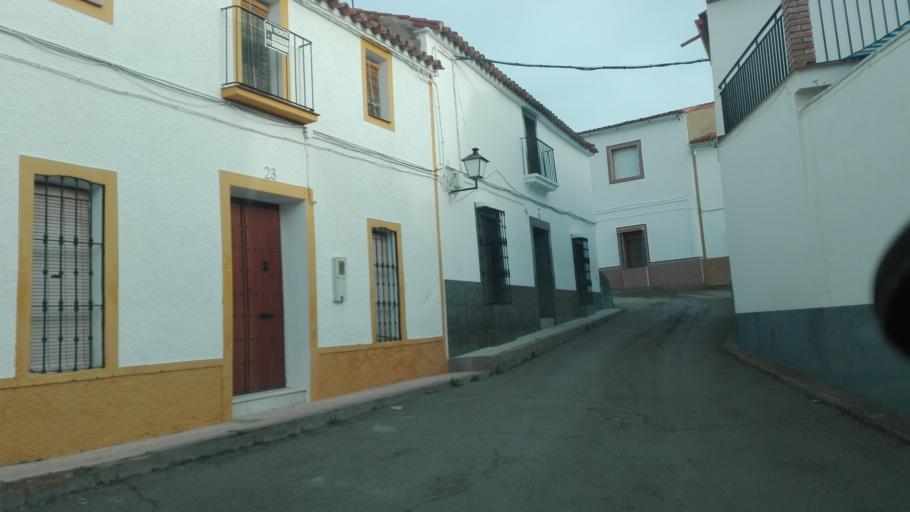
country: ES
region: Extremadura
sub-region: Provincia de Badajoz
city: Llera
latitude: 38.4478
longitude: -6.0557
